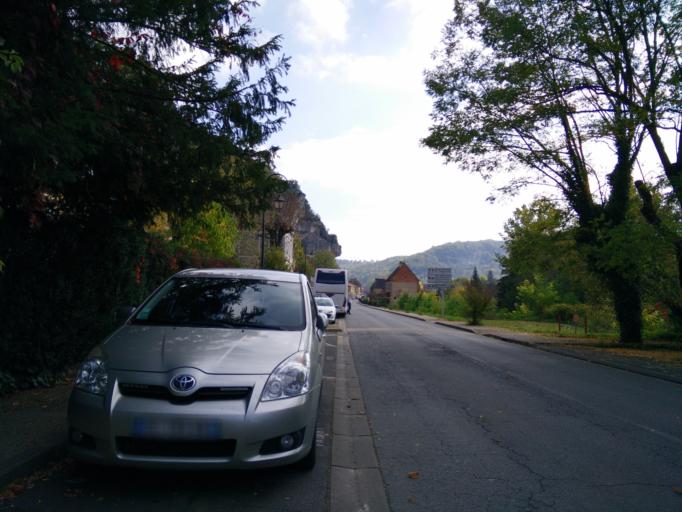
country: FR
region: Aquitaine
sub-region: Departement de la Dordogne
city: Saint-Cyprien
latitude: 44.9398
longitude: 1.0101
